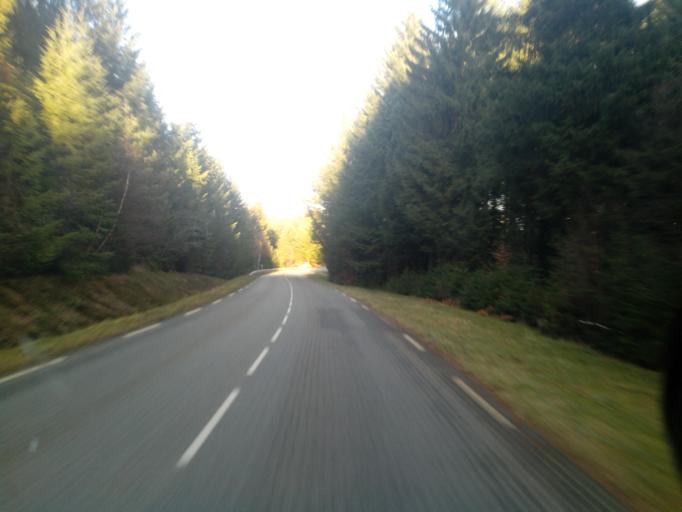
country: FR
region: Limousin
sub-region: Departement de la Correze
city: Meymac
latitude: 45.5749
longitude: 2.0924
